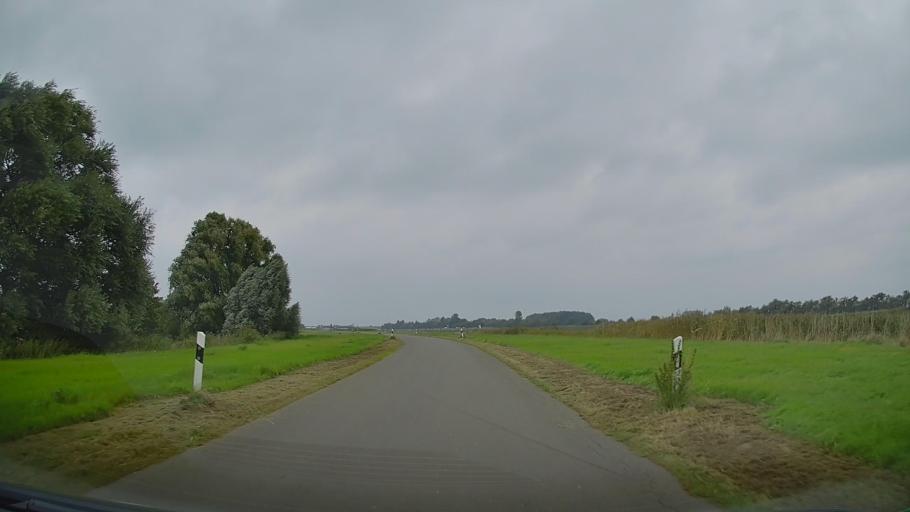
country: DE
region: Lower Saxony
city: Neuhaus an der Oste
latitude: 53.8122
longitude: 9.0431
